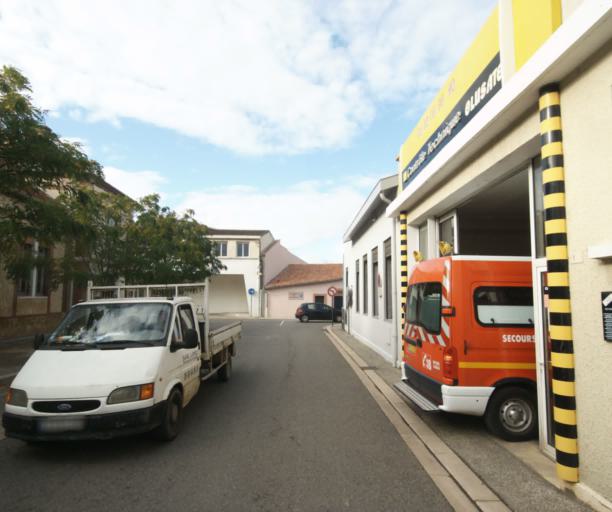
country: FR
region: Midi-Pyrenees
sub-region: Departement du Gers
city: Eauze
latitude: 43.8596
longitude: 0.1028
